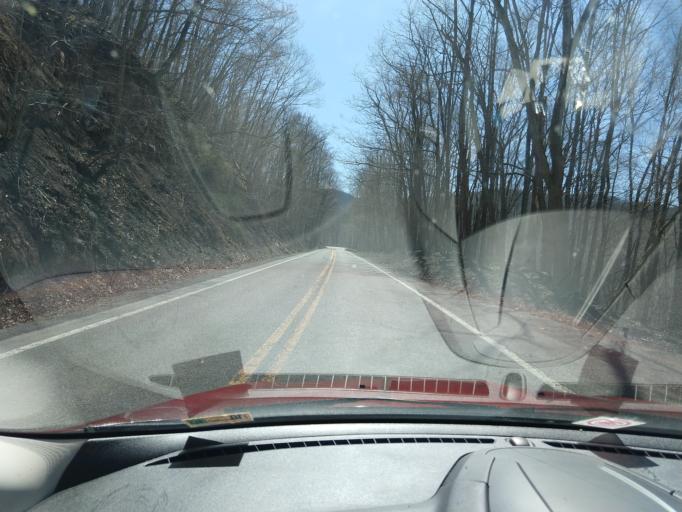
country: US
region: West Virginia
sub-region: Summers County
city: Hinton
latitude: 37.7463
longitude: -80.9164
